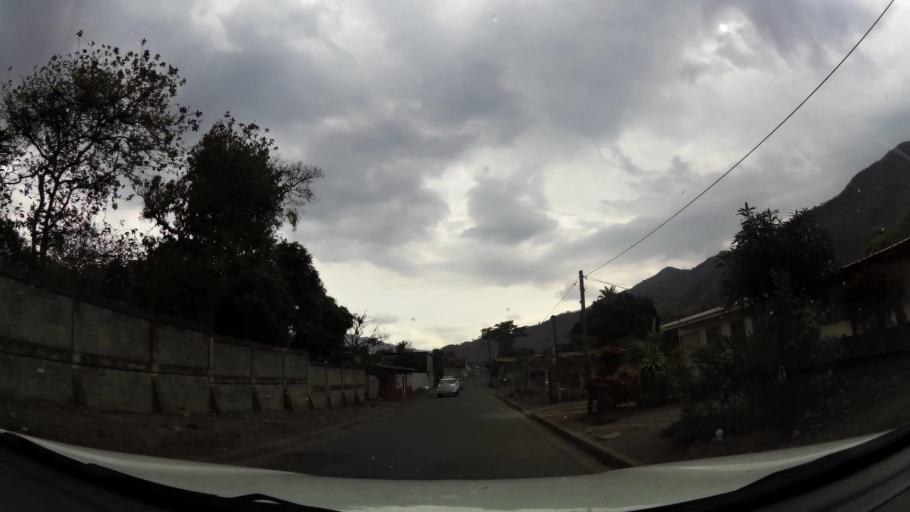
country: NI
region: Jinotega
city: Jinotega
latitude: 13.0940
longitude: -86.0046
